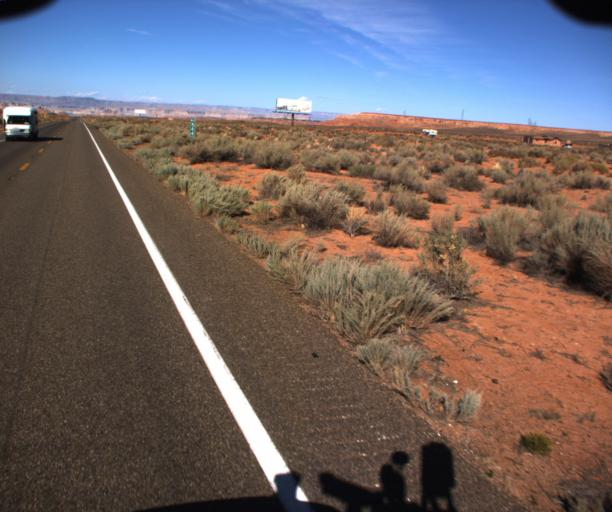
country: US
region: Arizona
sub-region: Coconino County
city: Page
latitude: 36.8650
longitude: -111.5041
